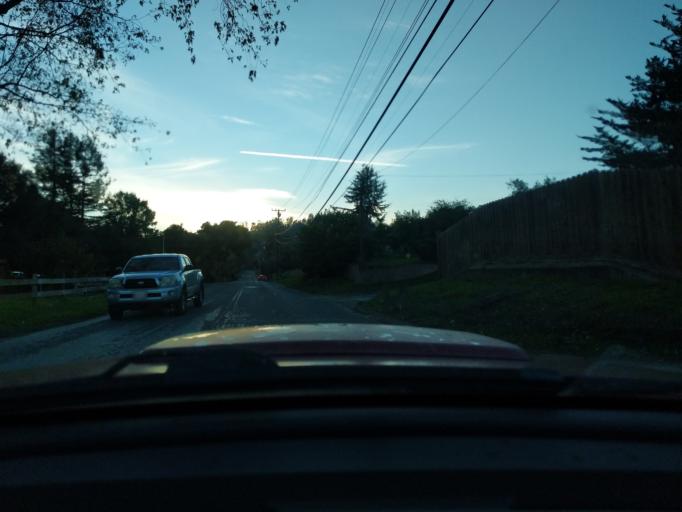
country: US
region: California
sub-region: Monterey County
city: Prunedale
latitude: 36.8242
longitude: -121.6671
